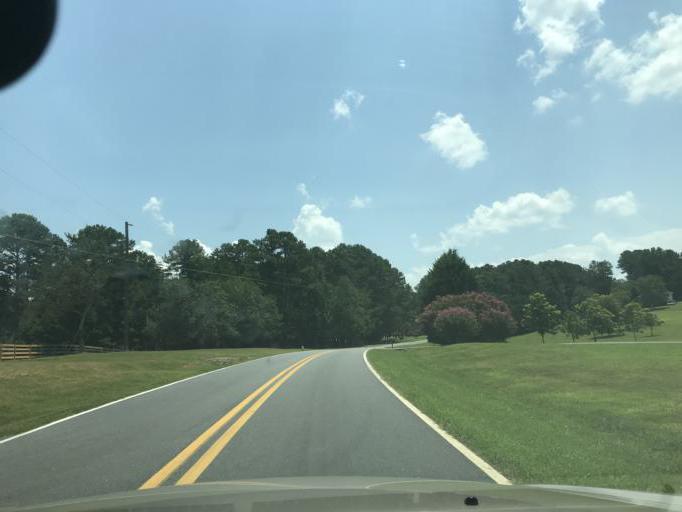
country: US
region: Georgia
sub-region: Forsyth County
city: Cumming
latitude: 34.3083
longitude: -84.1870
